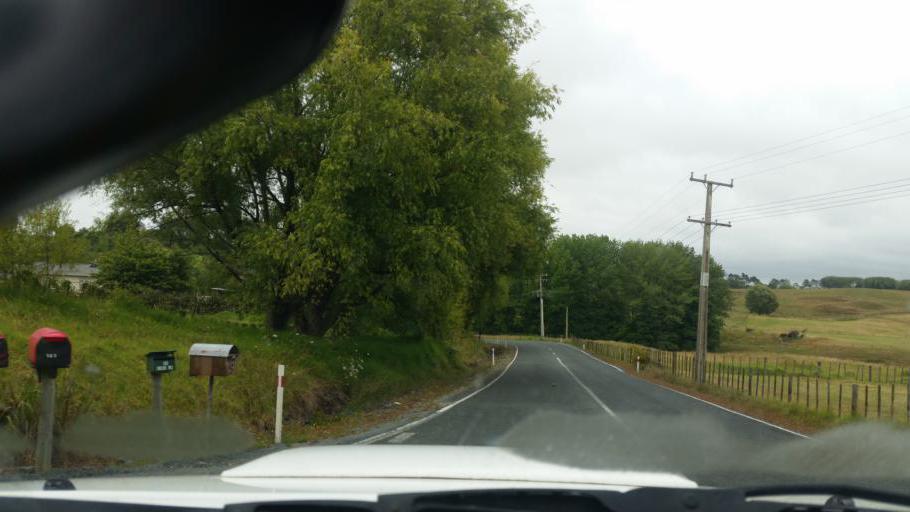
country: NZ
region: Auckland
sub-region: Auckland
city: Wellsford
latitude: -36.1706
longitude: 174.4626
